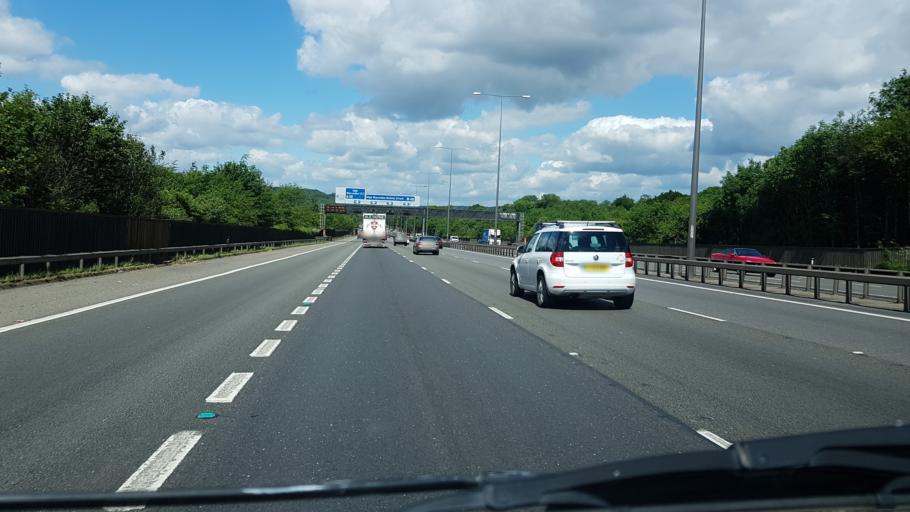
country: GB
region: England
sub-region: Buckinghamshire
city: Beaconsfield
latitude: 51.5996
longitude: -0.6804
